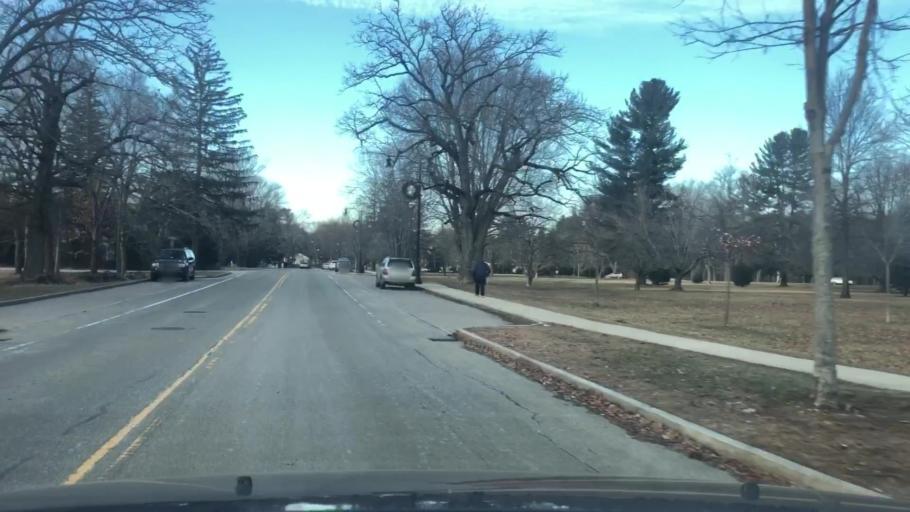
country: US
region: Massachusetts
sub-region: Essex County
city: North Andover
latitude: 42.6833
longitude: -71.1156
